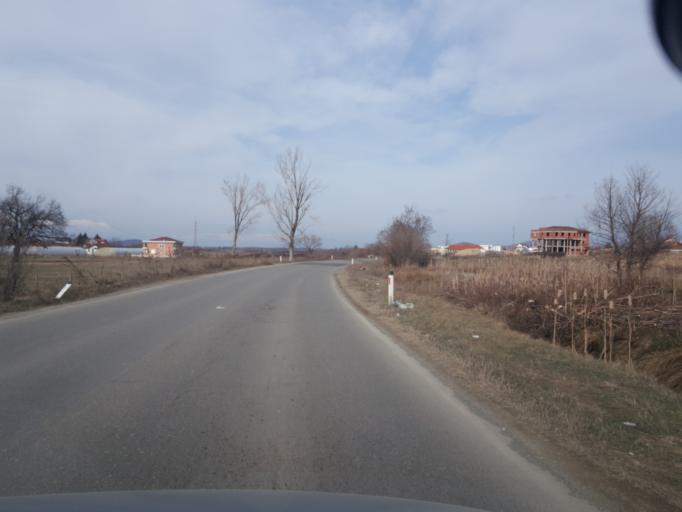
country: XK
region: Gjakova
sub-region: Komuna e Gjakoves
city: Gjakove
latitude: 42.4112
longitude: 20.4318
